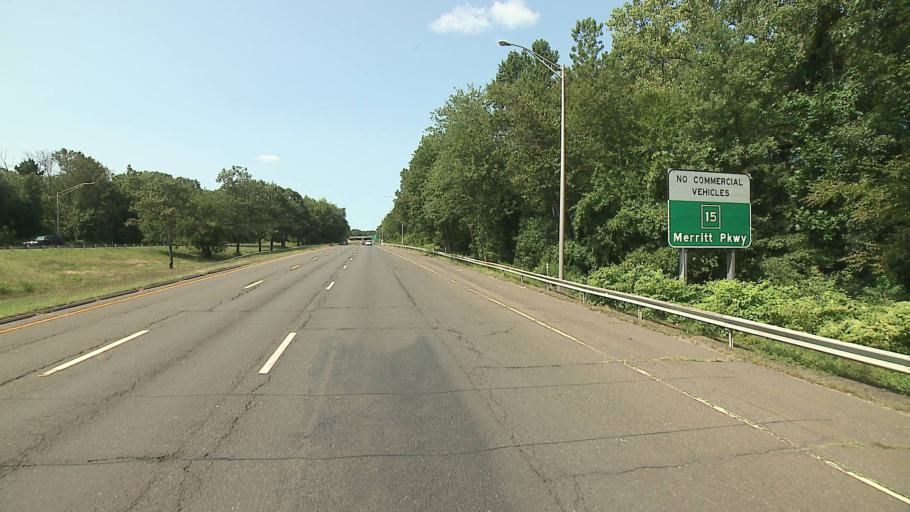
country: US
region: Connecticut
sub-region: Fairfield County
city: Trumbull
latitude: 41.2254
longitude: -73.1830
